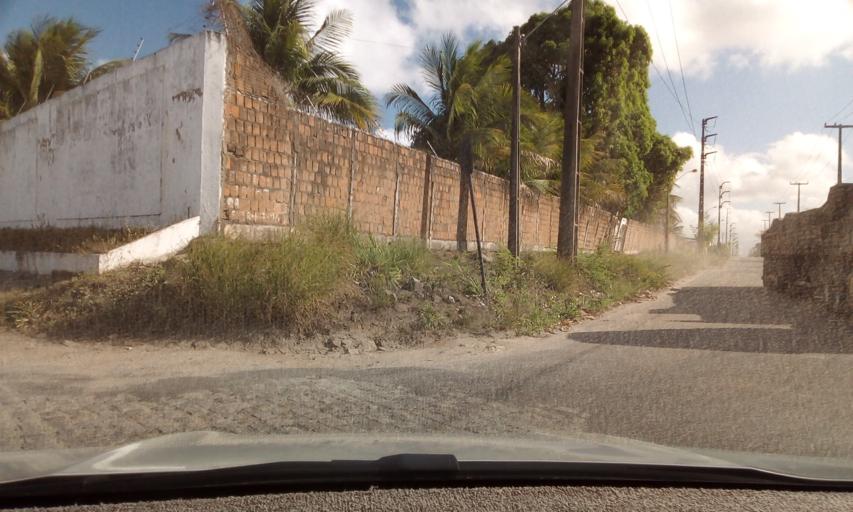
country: BR
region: Paraiba
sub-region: Bayeux
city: Bayeux
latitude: -7.1696
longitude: -34.9058
